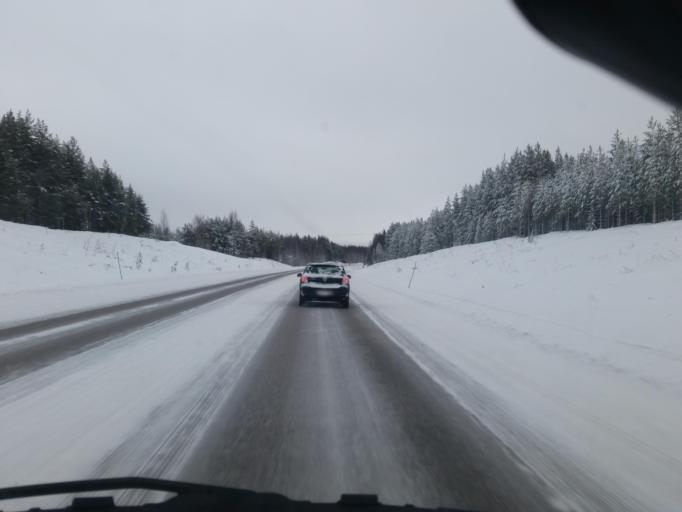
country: SE
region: Norrbotten
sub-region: Pitea Kommun
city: Bergsviken
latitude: 65.3180
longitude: 21.3751
